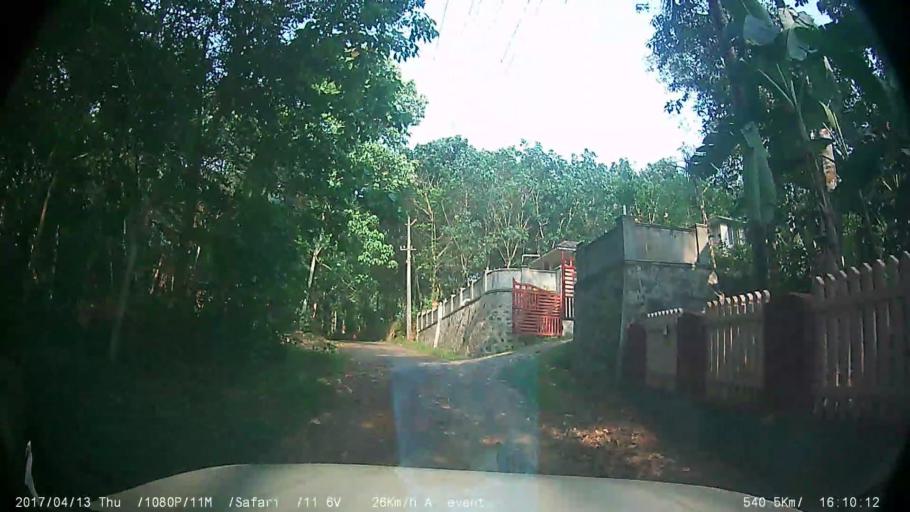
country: IN
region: Kerala
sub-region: Ernakulam
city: Piravam
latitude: 9.8231
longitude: 76.5160
